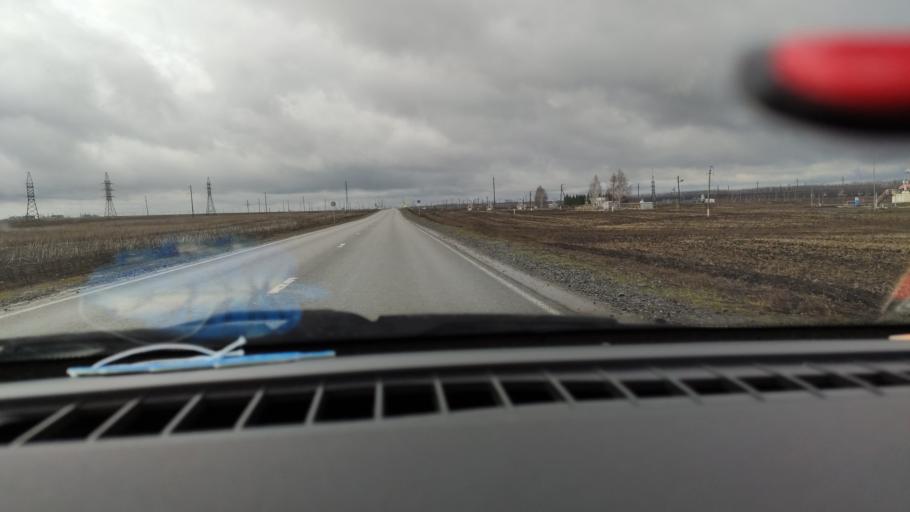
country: RU
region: Tatarstan
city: Nurlat
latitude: 54.4785
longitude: 50.8436
